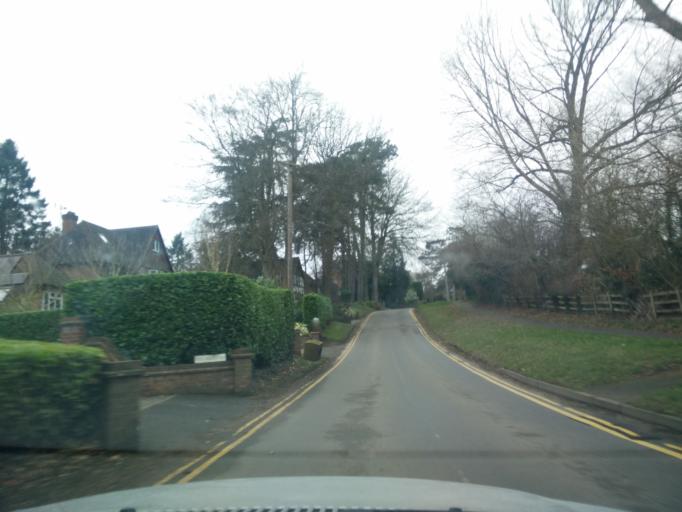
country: GB
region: England
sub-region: Buckinghamshire
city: Little Chalfont
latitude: 51.6628
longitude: -0.5614
